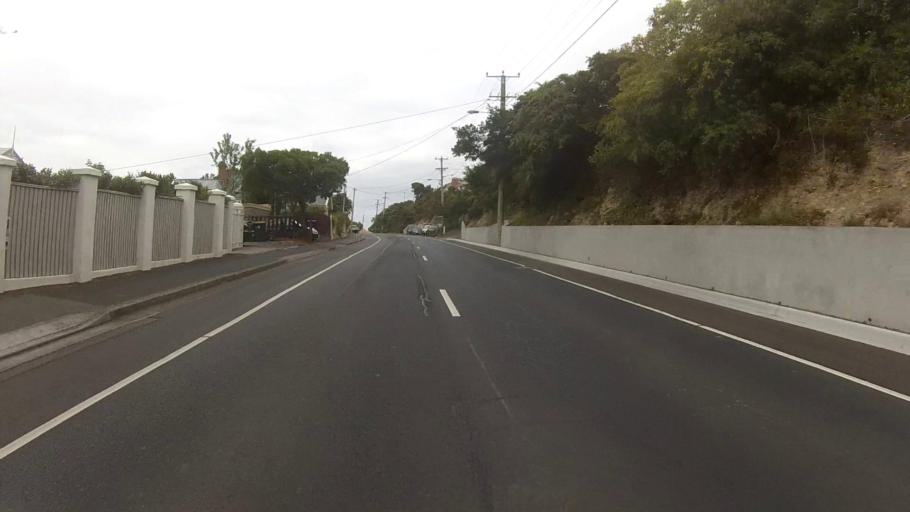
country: AU
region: Tasmania
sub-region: Kingborough
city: Taroona
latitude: -42.9218
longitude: 147.3600
